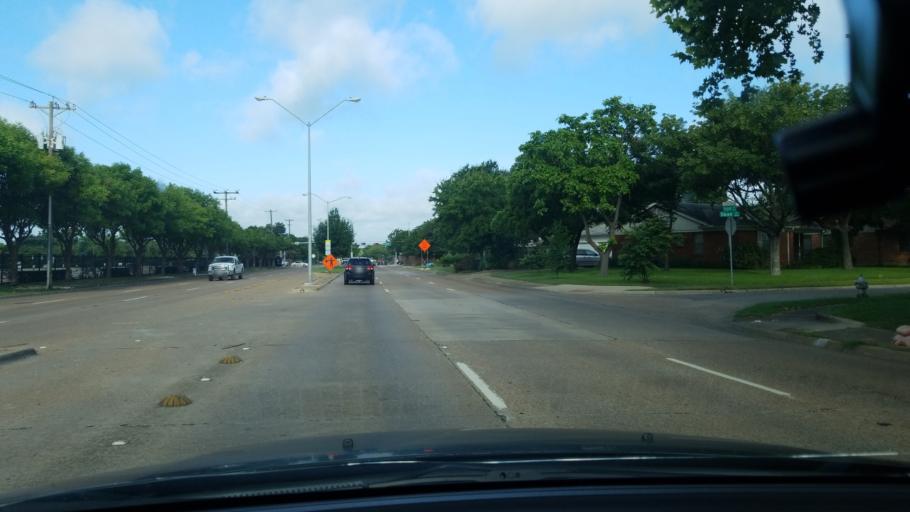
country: US
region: Texas
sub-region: Dallas County
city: Mesquite
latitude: 32.8192
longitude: -96.6825
